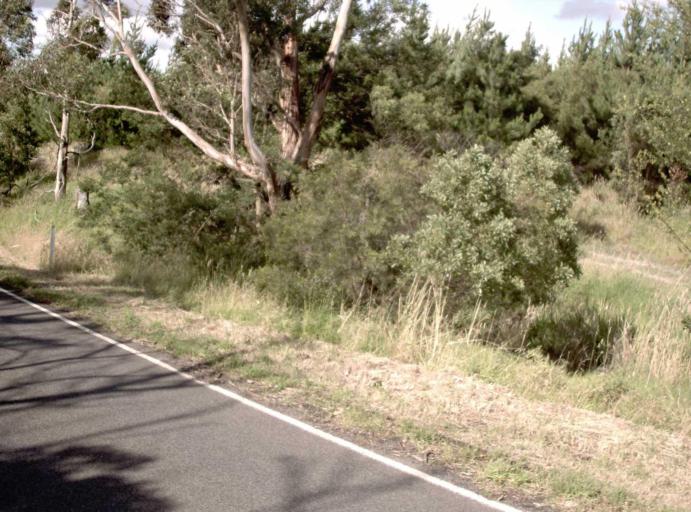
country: AU
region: Victoria
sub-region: Latrobe
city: Morwell
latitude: -38.1810
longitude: 146.4045
